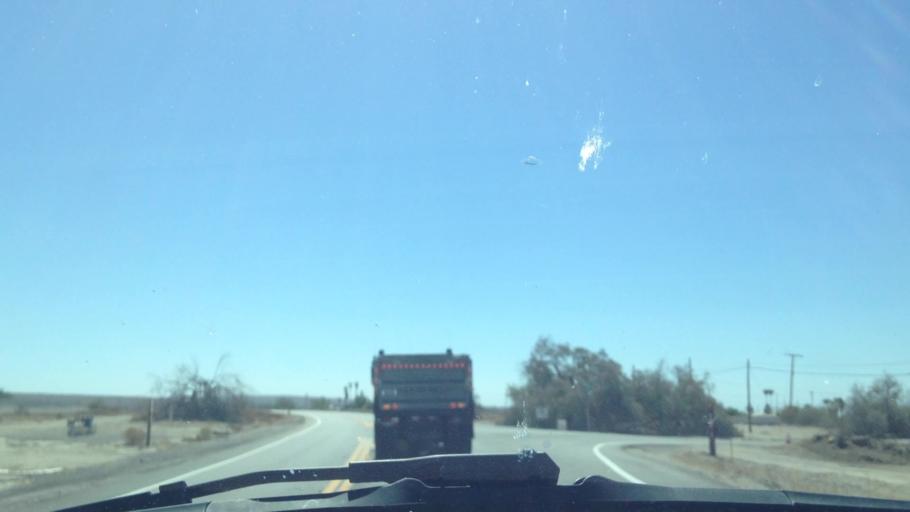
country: US
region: California
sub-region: Imperial County
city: Desert Shores
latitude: 33.5168
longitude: -115.9310
